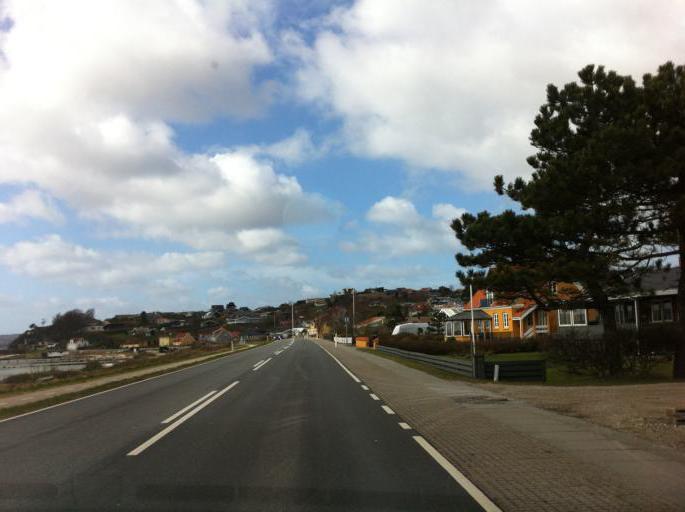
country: DK
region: Central Jutland
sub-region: Syddjurs Kommune
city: Ebeltoft
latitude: 56.2253
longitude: 10.6590
